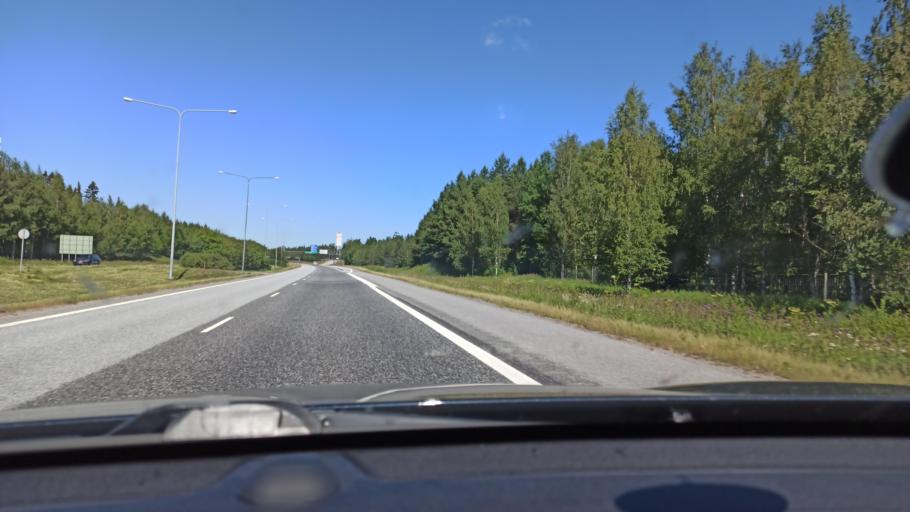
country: FI
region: Ostrobothnia
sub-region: Vaasa
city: Ristinummi
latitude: 63.0651
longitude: 21.7051
